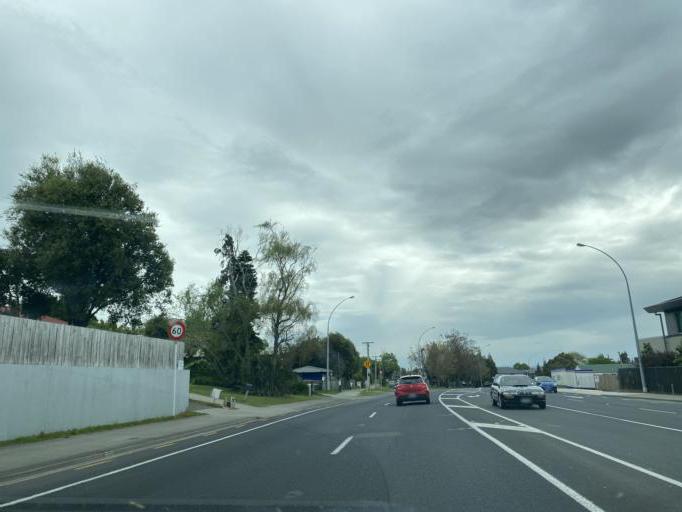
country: NZ
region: Waikato
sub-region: Hamilton City
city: Hamilton
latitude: -37.8084
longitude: 175.2798
